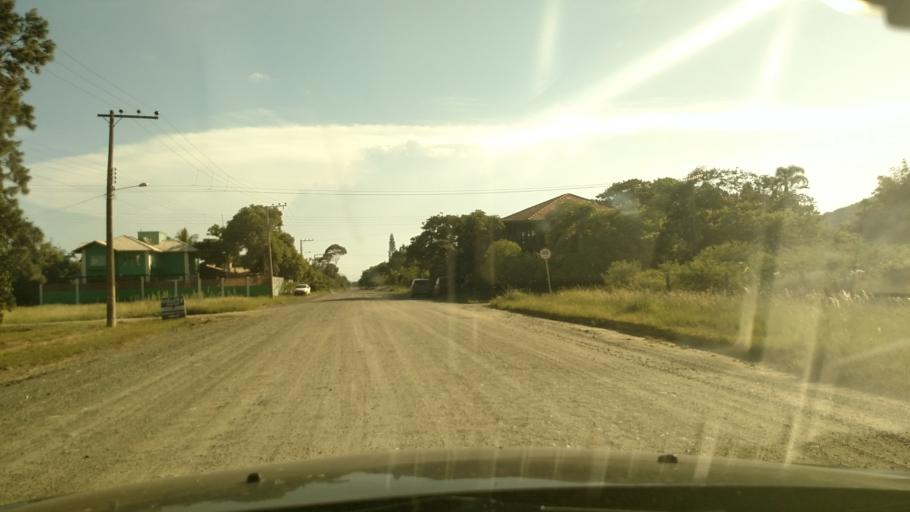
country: BR
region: Santa Catarina
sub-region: Porto Belo
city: Porto Belo
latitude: -27.1701
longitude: -48.5019
